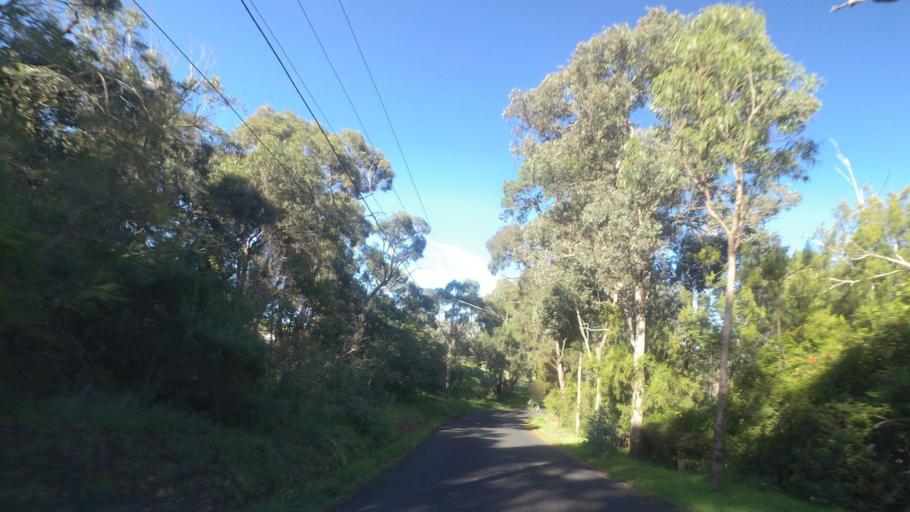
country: AU
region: Victoria
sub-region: Nillumbik
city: Research
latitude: -37.7039
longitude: 145.1941
